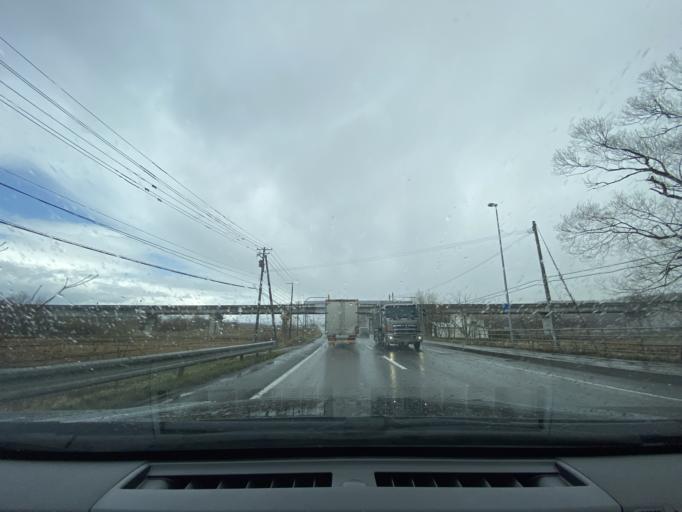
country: JP
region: Hokkaido
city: Fukagawa
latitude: 43.6734
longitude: 142.0207
